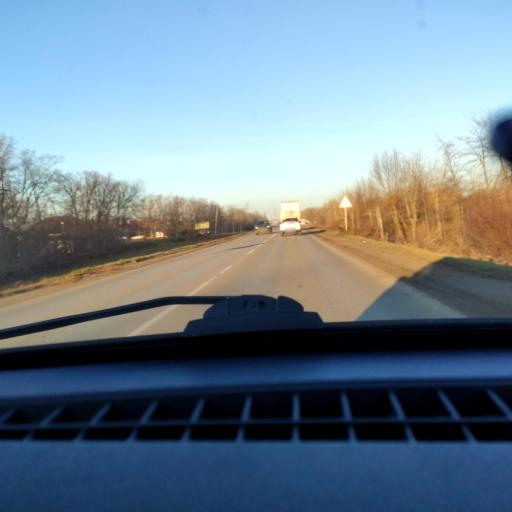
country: RU
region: Bashkortostan
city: Ufa
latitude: 54.6251
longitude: 55.9131
